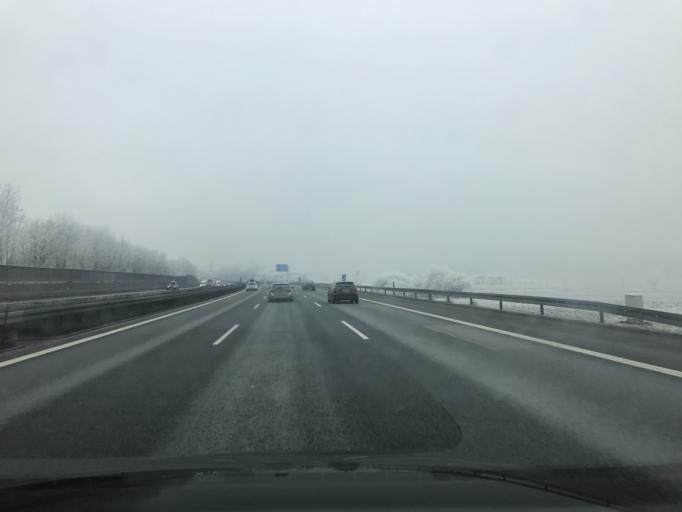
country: DE
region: Bavaria
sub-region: Upper Bavaria
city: Denkendorf
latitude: 48.9249
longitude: 11.4670
